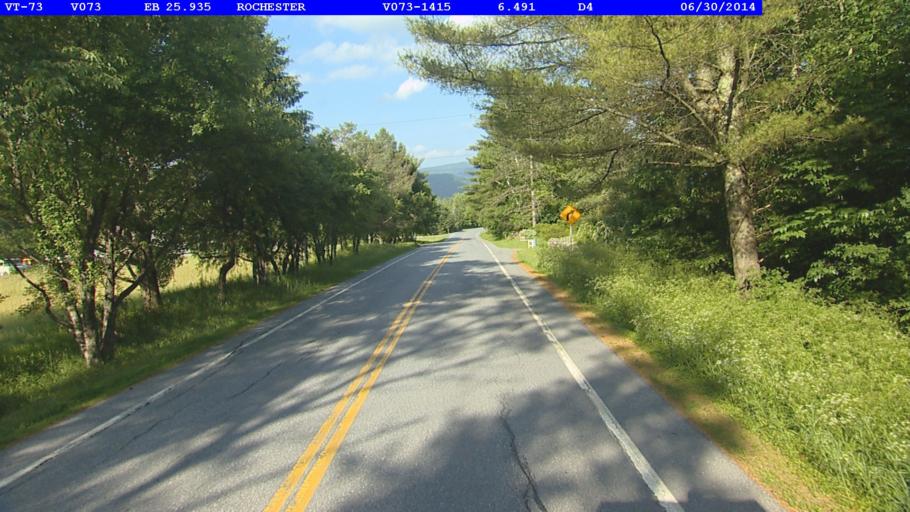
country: US
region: Vermont
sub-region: Orange County
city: Randolph
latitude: 43.8489
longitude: -72.8469
